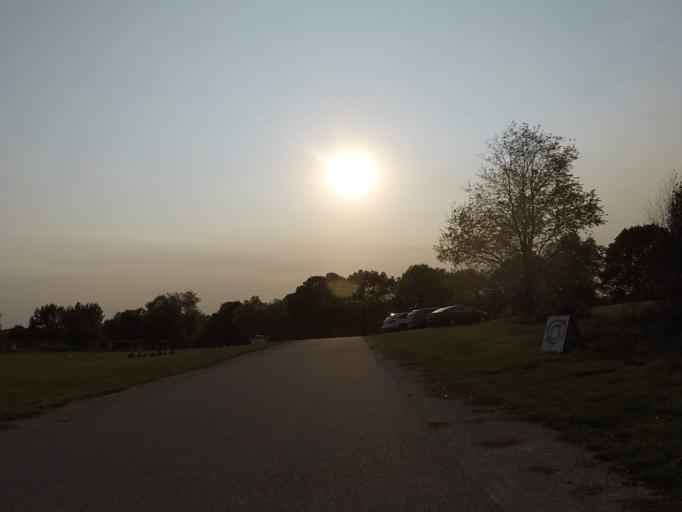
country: US
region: Wisconsin
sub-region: Dane County
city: Verona
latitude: 43.0010
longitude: -89.5253
